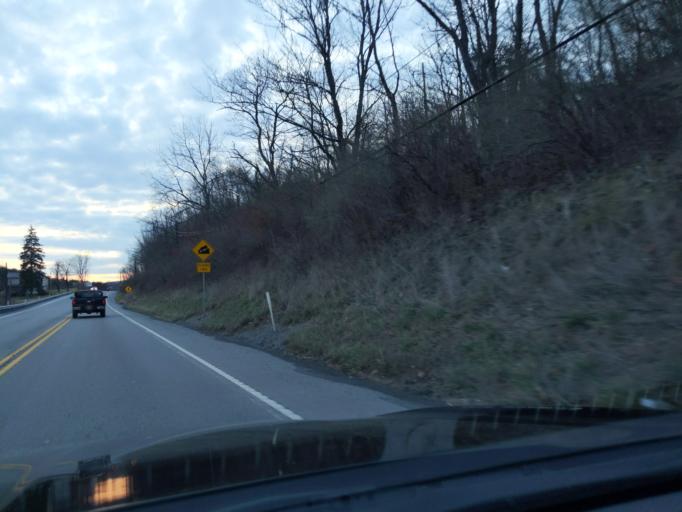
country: US
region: Pennsylvania
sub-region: Blair County
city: Lakemont
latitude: 40.4578
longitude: -78.3238
